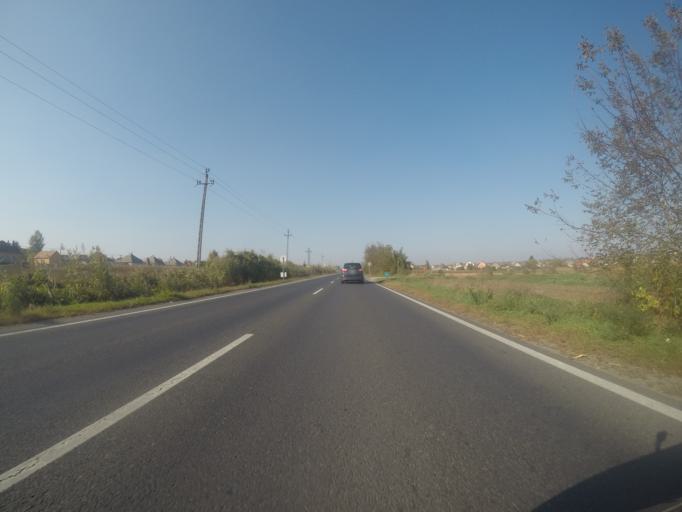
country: HU
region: Tolna
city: Dunafoldvar
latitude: 46.8060
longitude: 18.9147
